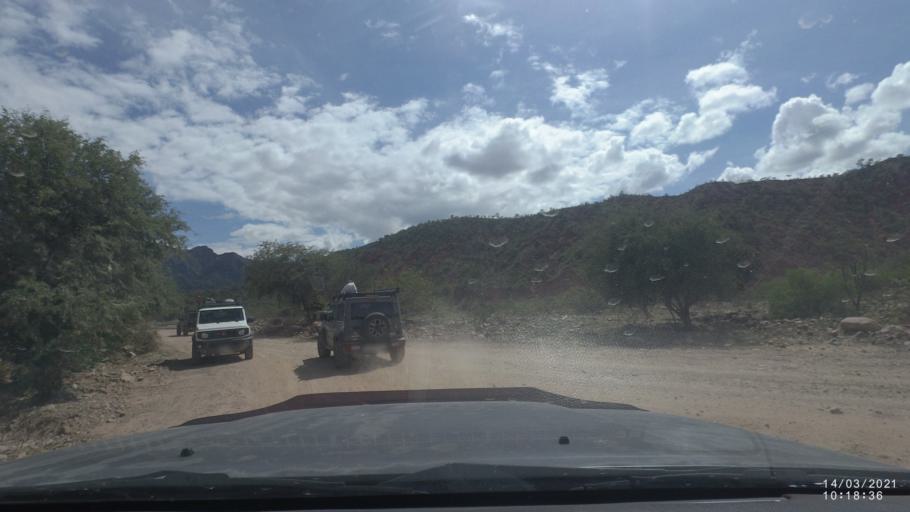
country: BO
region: Cochabamba
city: Cliza
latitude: -17.9344
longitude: -65.8678
